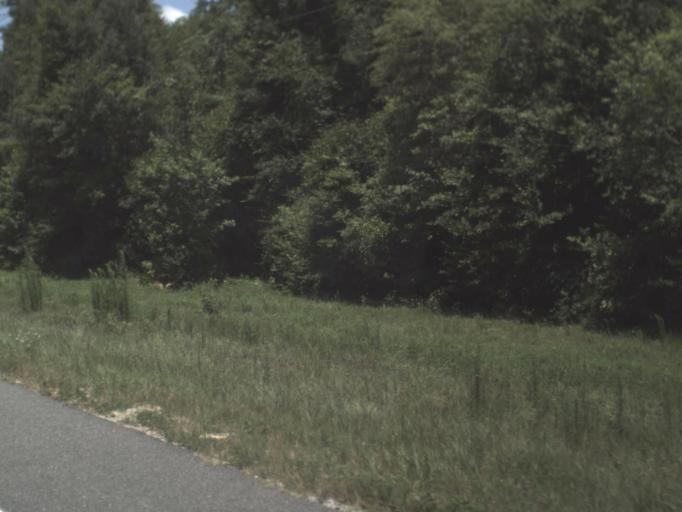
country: US
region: Florida
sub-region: Levy County
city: Manatee Road
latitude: 29.6229
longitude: -82.9832
